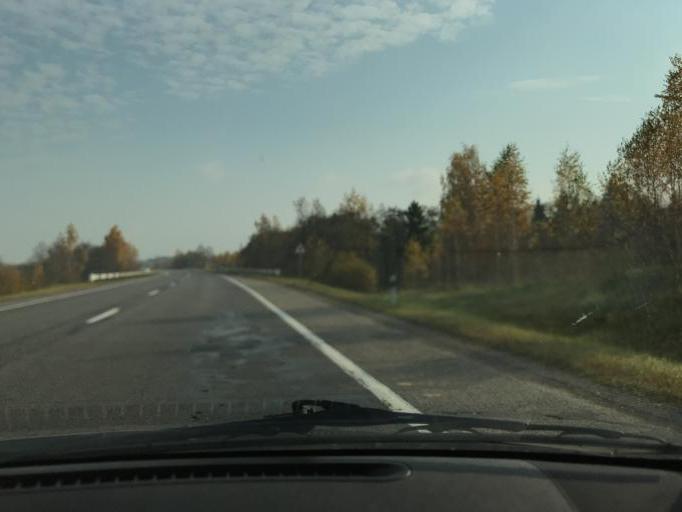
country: BY
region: Vitebsk
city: Lyepyel'
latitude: 54.9890
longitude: 28.8891
